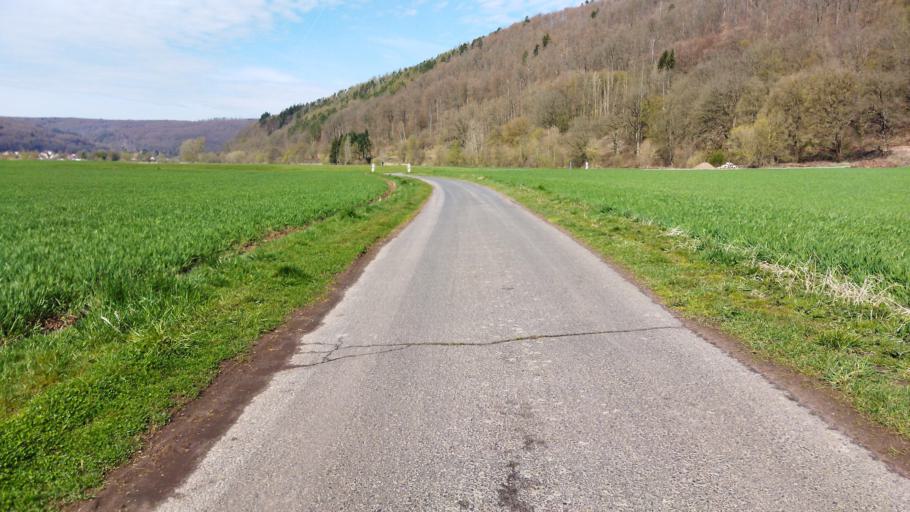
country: DE
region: Lower Saxony
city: Bodenfelde
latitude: 51.5987
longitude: 9.5772
